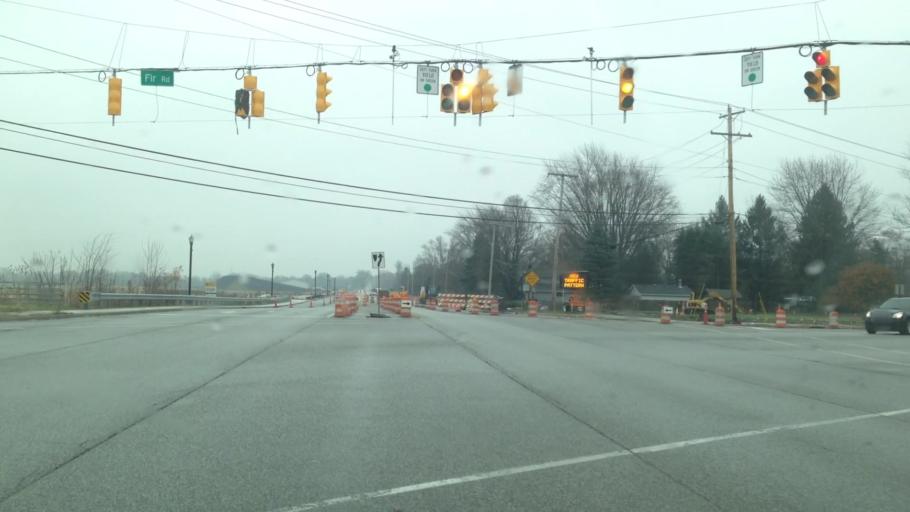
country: US
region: Indiana
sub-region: Saint Joseph County
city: Mishawaka
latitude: 41.7096
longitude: -86.1610
